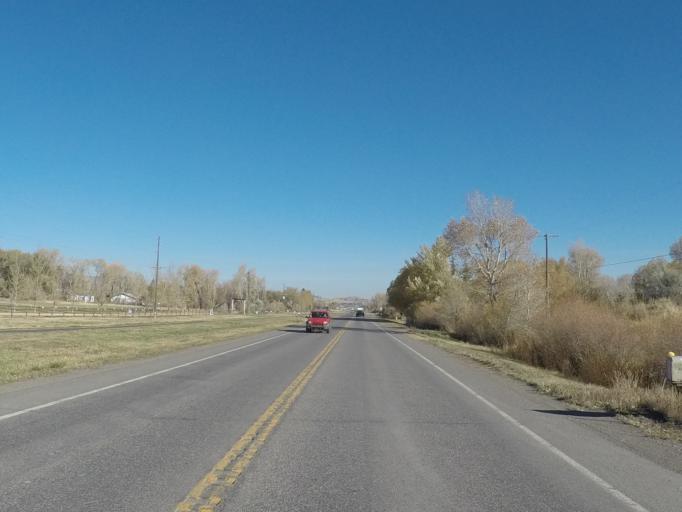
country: US
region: Montana
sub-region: Park County
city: Livingston
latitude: 45.6250
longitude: -110.5779
